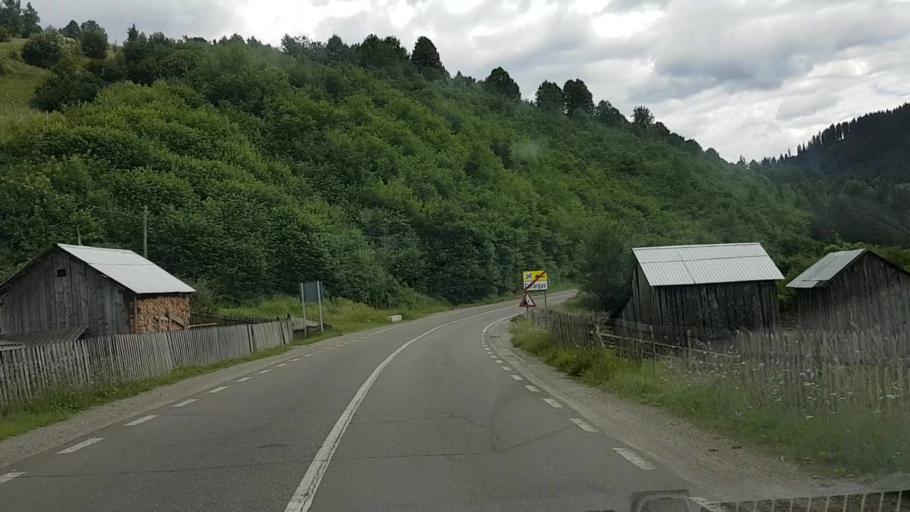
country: RO
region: Suceava
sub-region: Comuna Brosteni
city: Brosteni
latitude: 47.2356
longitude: 25.7422
